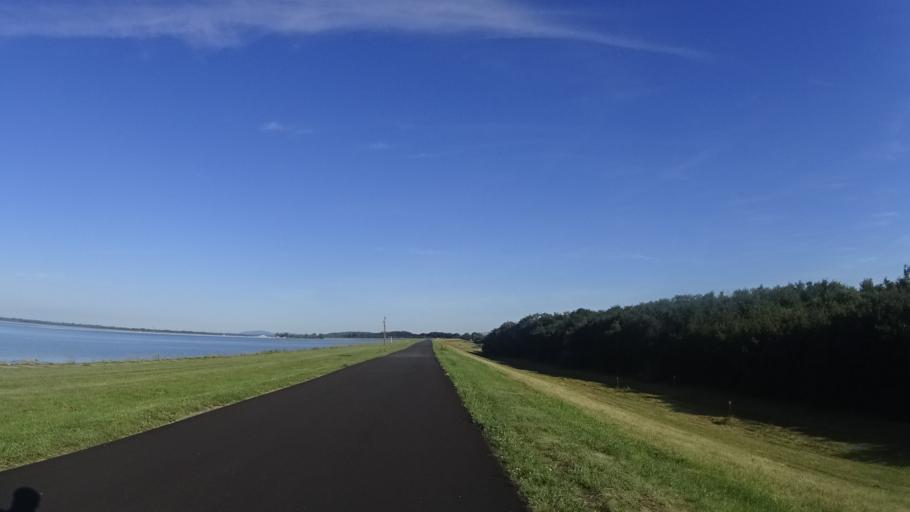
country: SK
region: Trnavsky
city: Samorin
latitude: 48.0117
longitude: 17.3008
